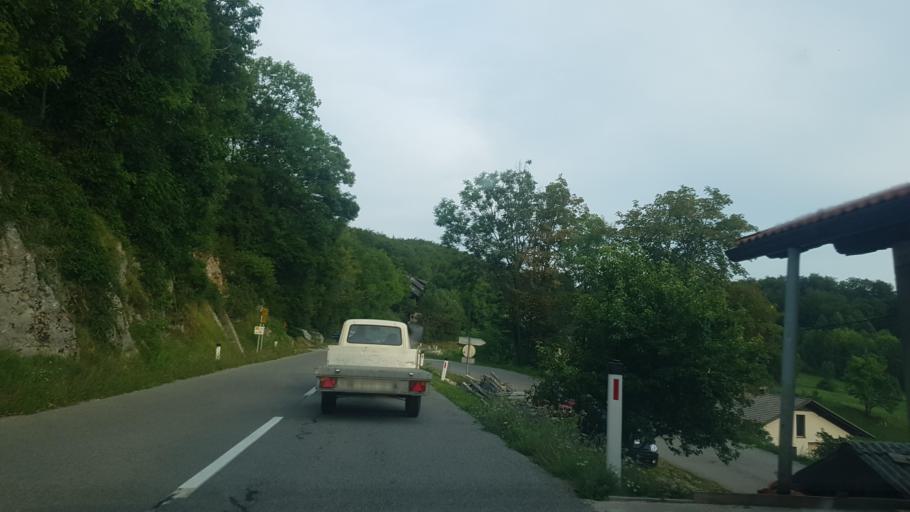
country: SI
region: Vipava
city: Vipava
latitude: 45.8642
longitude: 14.0620
